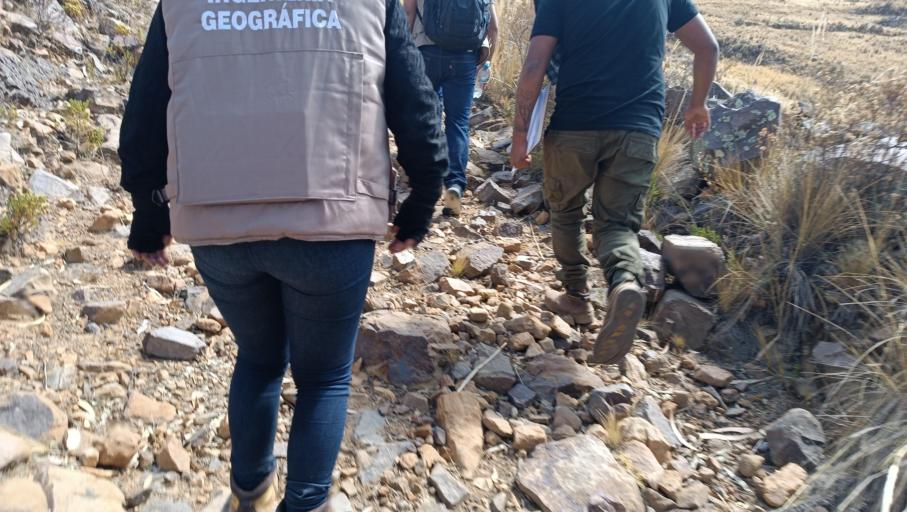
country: BO
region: La Paz
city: Batallas
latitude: -16.3496
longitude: -68.6492
